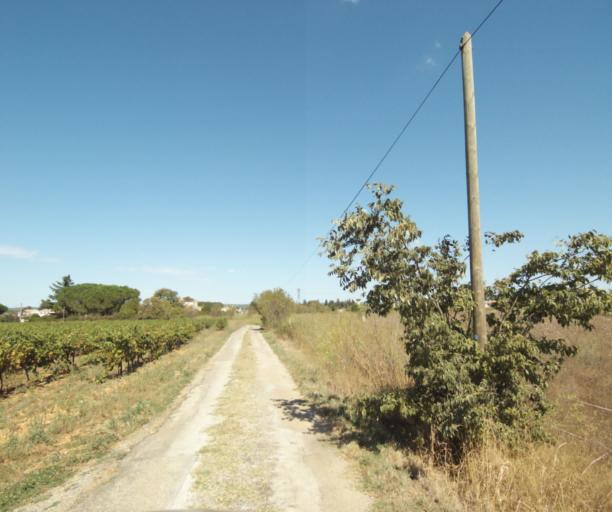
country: FR
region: Languedoc-Roussillon
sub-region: Departement du Gard
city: Rodilhan
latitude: 43.8193
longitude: 4.4352
